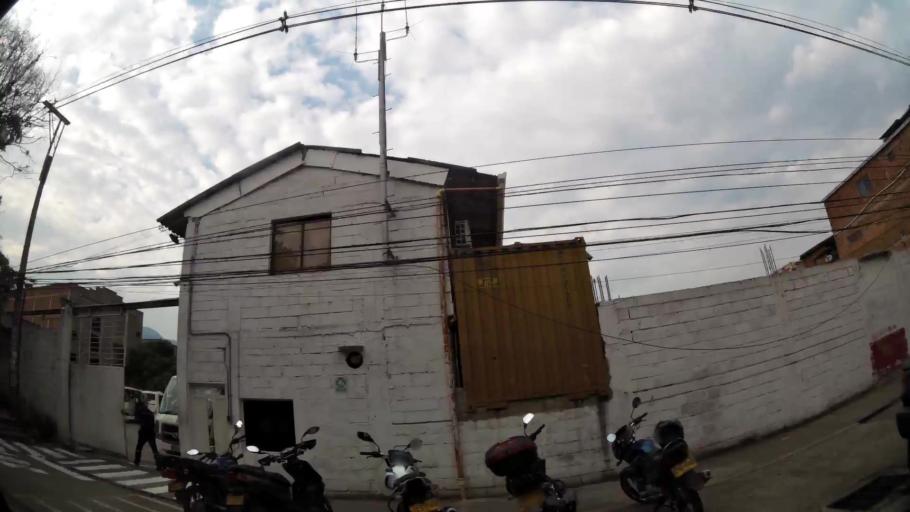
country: CO
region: Antioquia
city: Medellin
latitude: 6.2616
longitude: -75.5707
